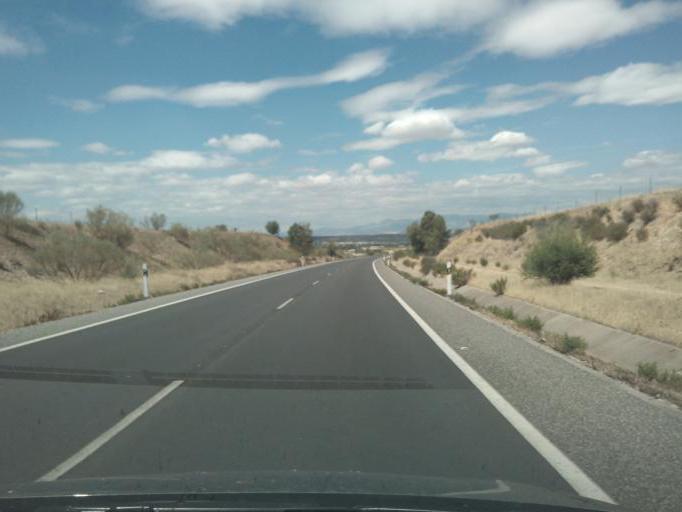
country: ES
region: Madrid
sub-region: Provincia de Madrid
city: Cobena
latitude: 40.5736
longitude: -3.5296
